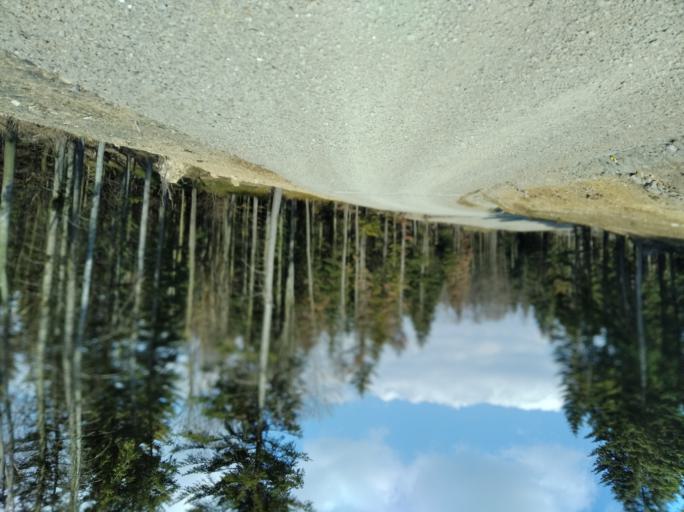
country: PL
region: Subcarpathian Voivodeship
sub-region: Powiat strzyzowski
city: Strzyzow
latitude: 49.8233
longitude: 21.8007
